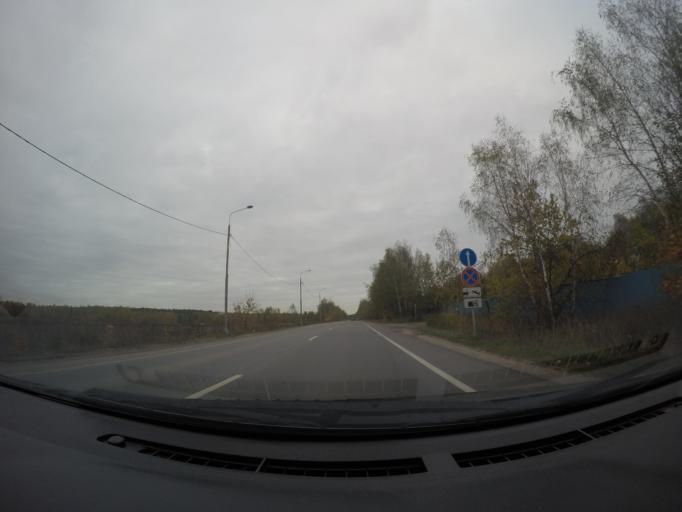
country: RU
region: Moskovskaya
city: Imeni Vorovskogo
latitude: 55.7217
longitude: 38.3813
